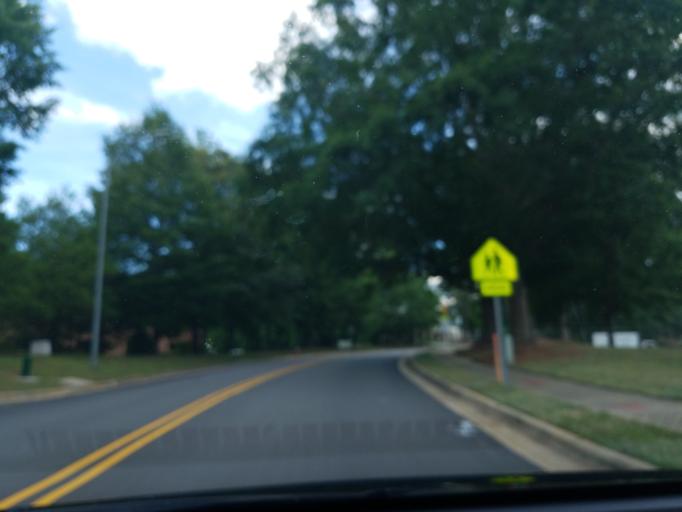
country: US
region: North Carolina
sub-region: Wake County
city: Apex
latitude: 35.7346
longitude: -78.8078
